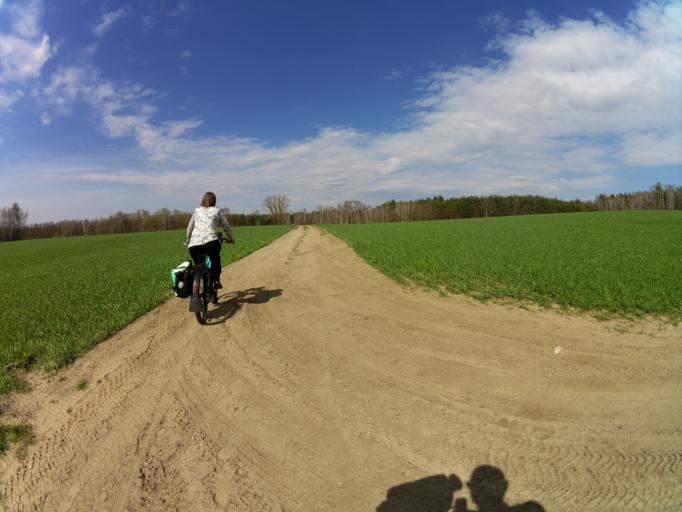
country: PL
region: West Pomeranian Voivodeship
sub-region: Powiat mysliborski
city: Mysliborz
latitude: 52.9425
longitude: 14.8629
